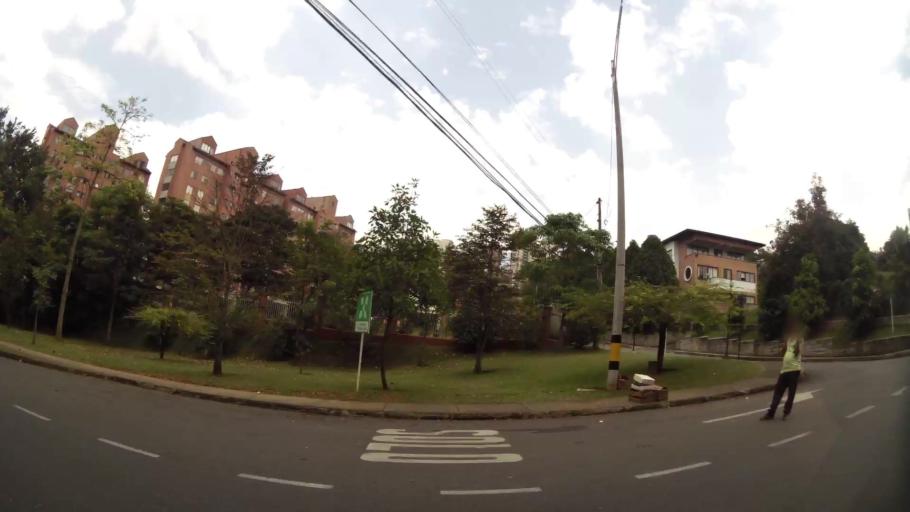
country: CO
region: Antioquia
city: Envigado
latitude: 6.1821
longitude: -75.5707
